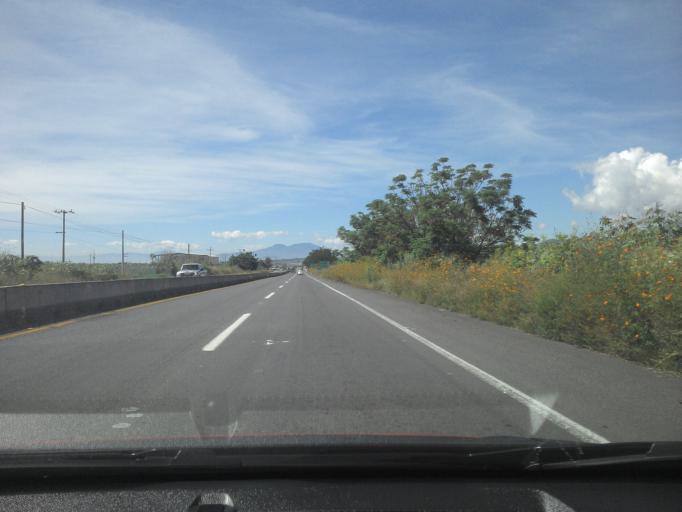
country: MX
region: Jalisco
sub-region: Tala
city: Los Ruisenores
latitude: 20.7146
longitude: -103.6490
